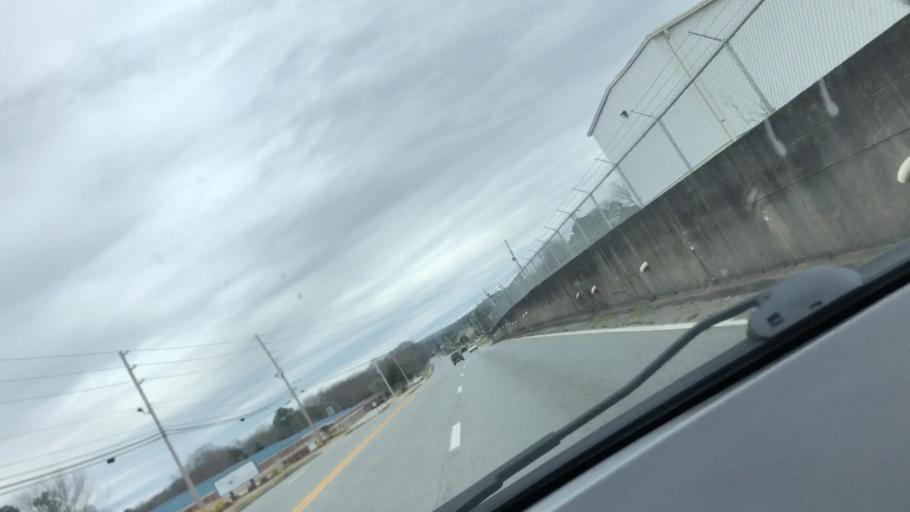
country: US
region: Georgia
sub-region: Bartow County
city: Cartersville
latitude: 34.2089
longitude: -84.8192
